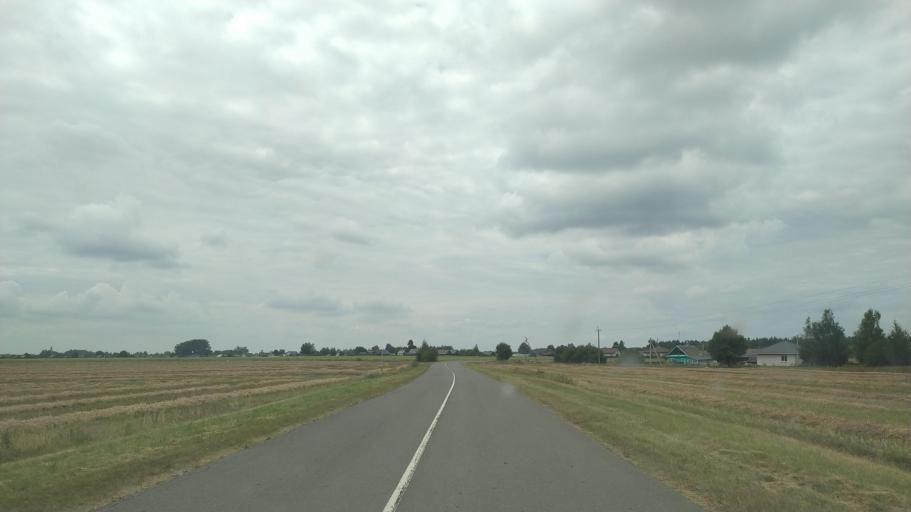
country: BY
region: Brest
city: Byelaazyorsk
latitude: 52.5408
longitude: 25.1157
